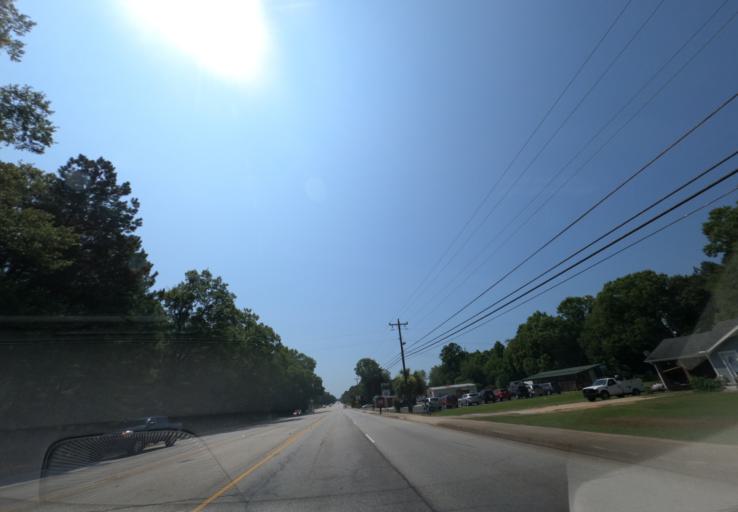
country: US
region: South Carolina
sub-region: Greenwood County
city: Greenwood
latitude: 34.1501
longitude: -82.1374
